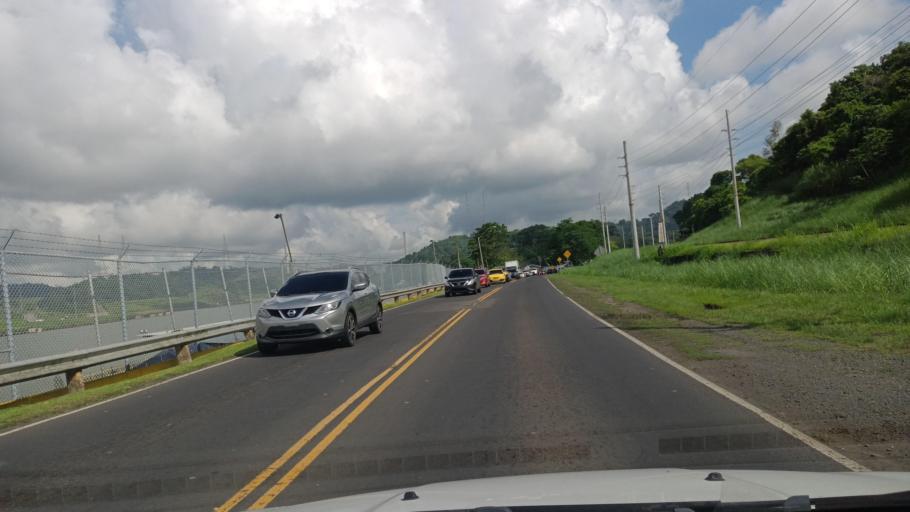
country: PA
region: Panama
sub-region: Distrito de Panama
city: Paraiso
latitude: 9.0217
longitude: -79.6151
